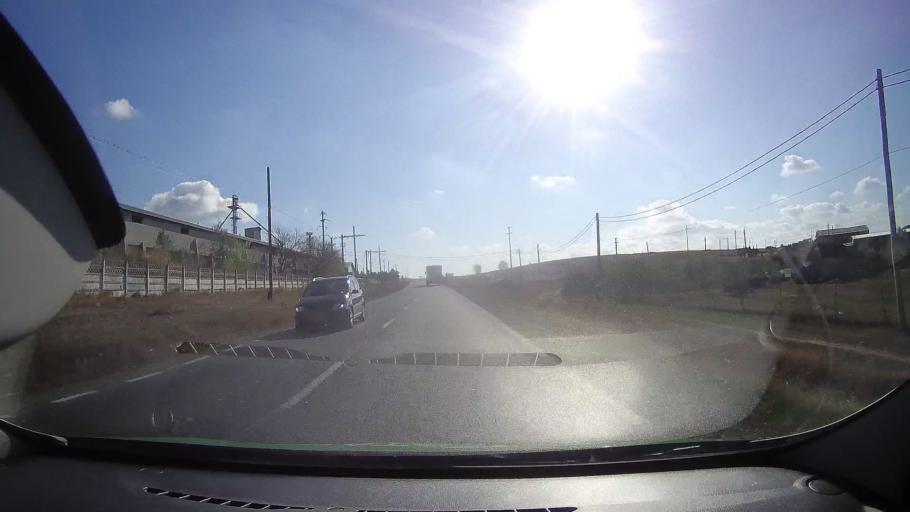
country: RO
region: Tulcea
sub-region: Comuna Baia
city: Baia
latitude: 44.7179
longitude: 28.6807
